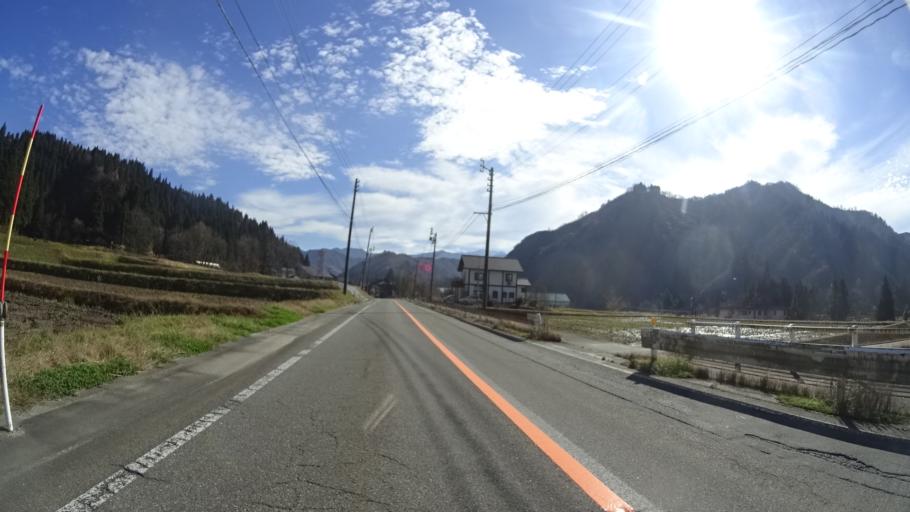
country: JP
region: Niigata
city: Muikamachi
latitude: 37.2116
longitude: 139.0556
